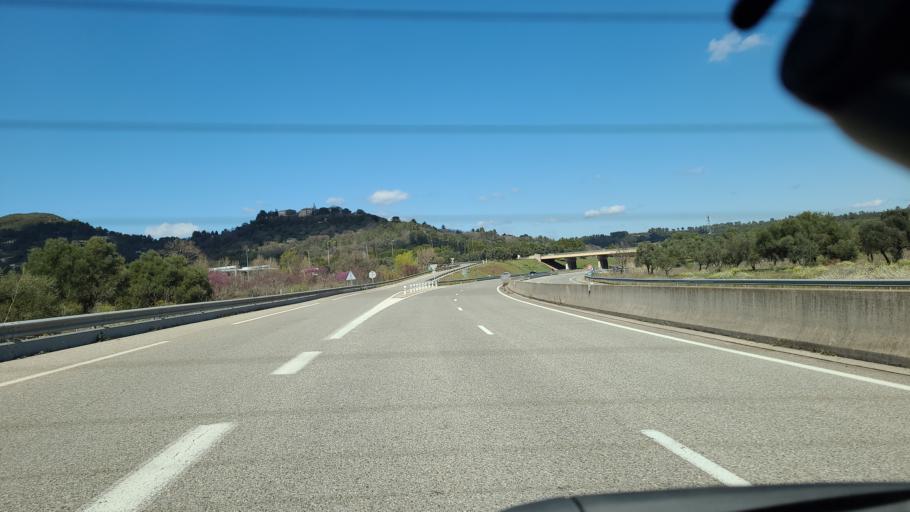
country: FR
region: Provence-Alpes-Cote d'Azur
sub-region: Departement du Var
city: Le Cannet-des-Maures
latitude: 43.3908
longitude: 6.3541
